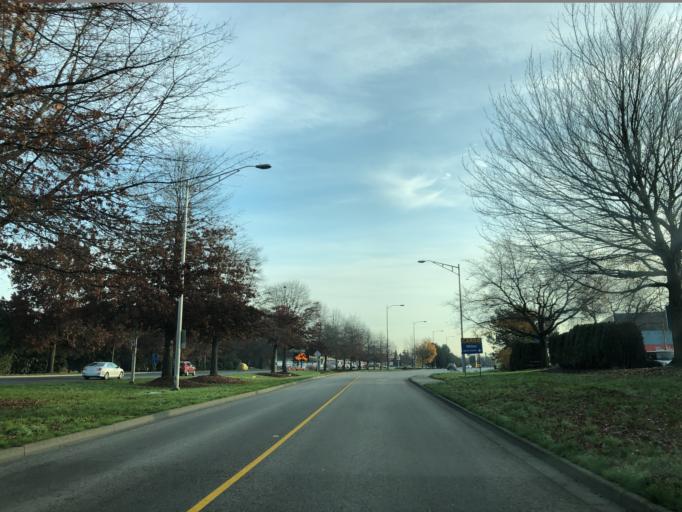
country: CA
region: British Columbia
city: Richmond
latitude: 49.1920
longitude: -123.1711
